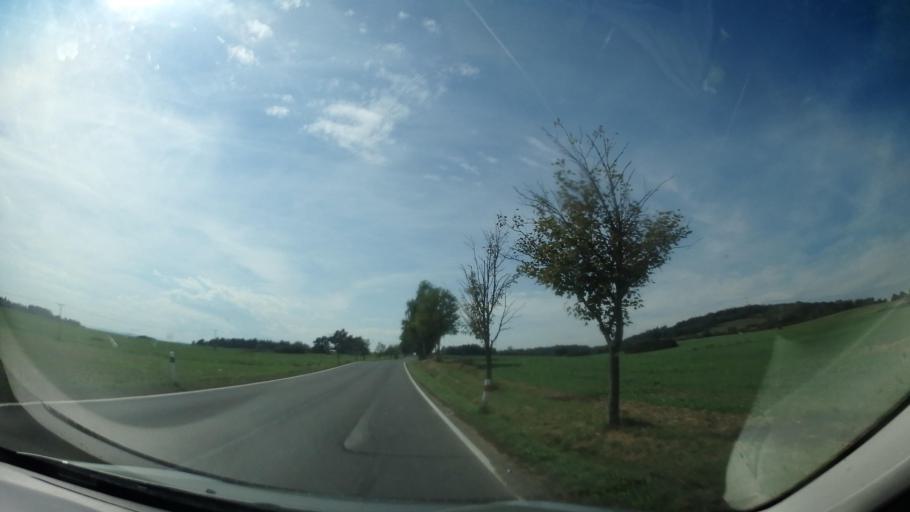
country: CZ
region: Jihocesky
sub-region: Okres Pisek
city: Pisek
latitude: 49.3065
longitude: 14.0808
